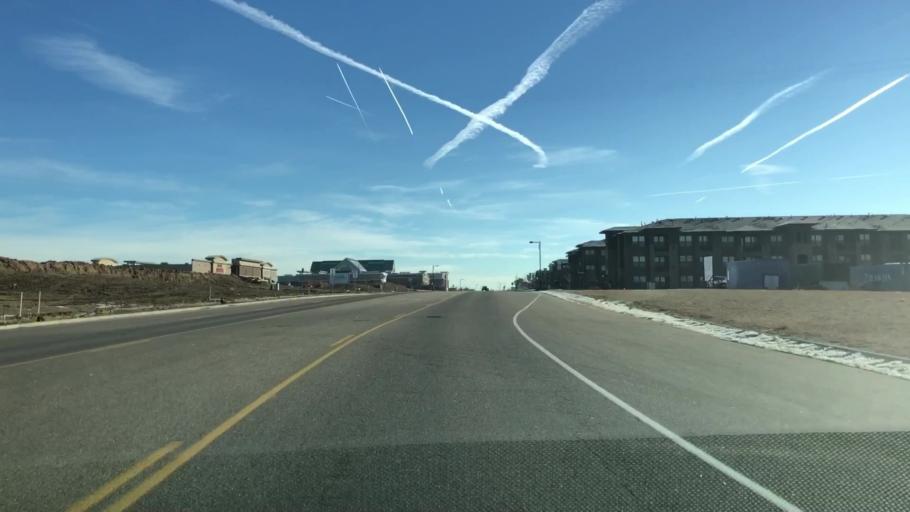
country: US
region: Colorado
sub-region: Larimer County
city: Loveland
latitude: 40.4034
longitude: -104.9875
